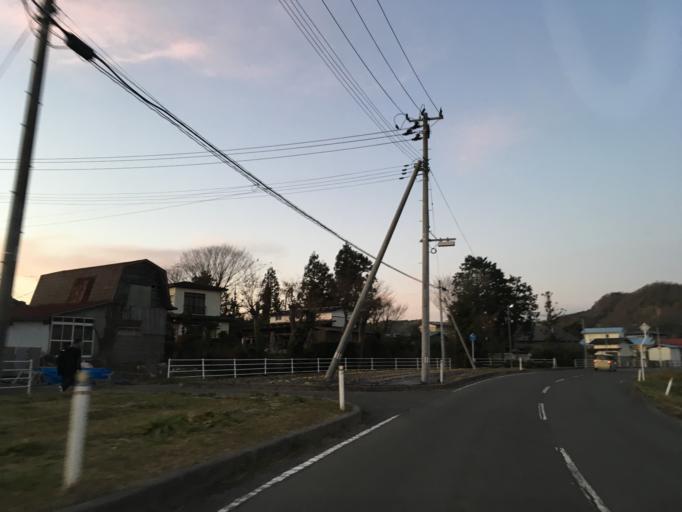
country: JP
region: Iwate
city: Ichinoseki
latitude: 38.7441
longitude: 141.2182
